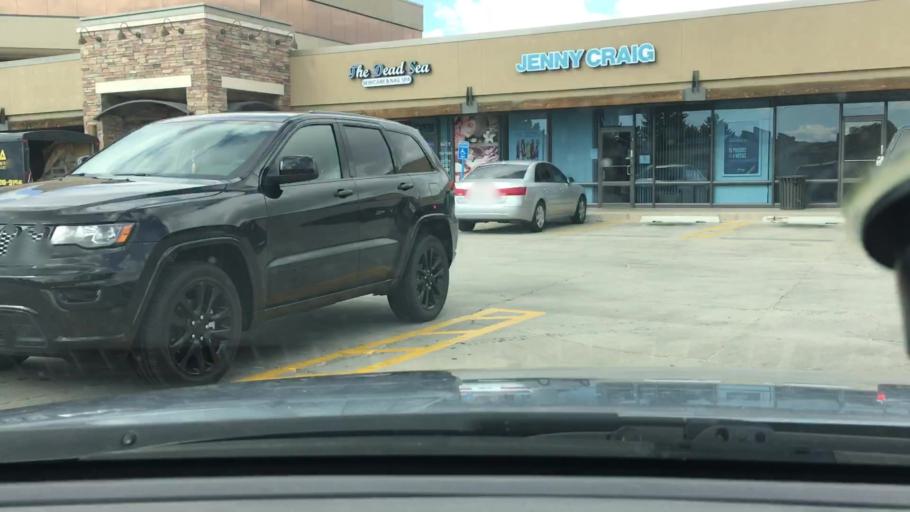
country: US
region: Utah
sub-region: Salt Lake County
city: South Salt Lake
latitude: 40.7258
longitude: -111.8722
